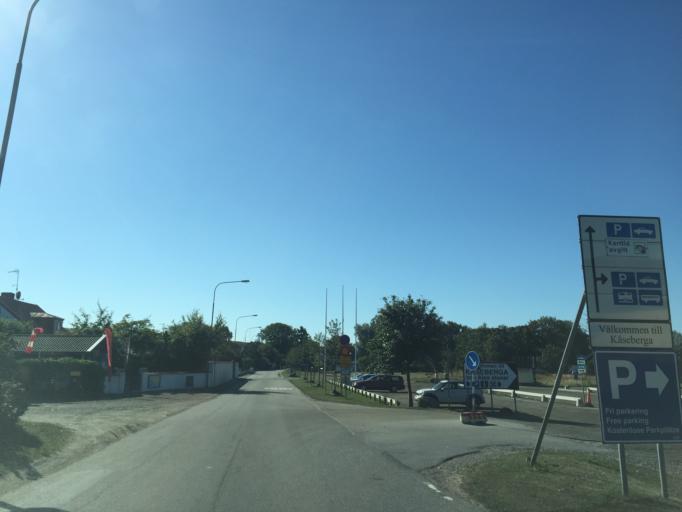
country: SE
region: Skane
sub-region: Ystads Kommun
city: Kopingebro
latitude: 55.3889
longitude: 14.0634
